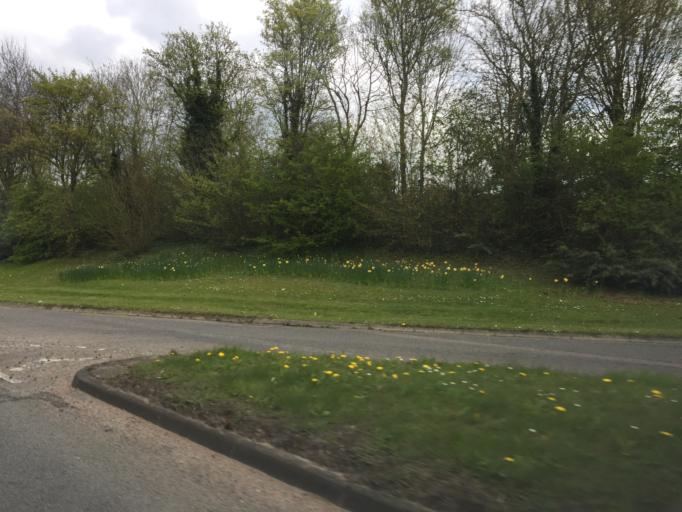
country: GB
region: England
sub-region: Milton Keynes
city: Milton Keynes
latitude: 52.0299
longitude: -0.7486
